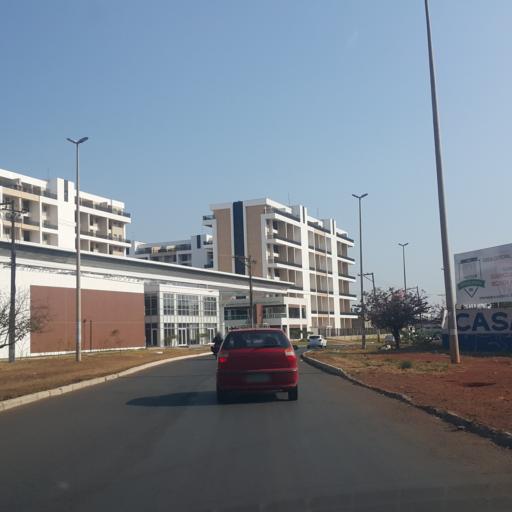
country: BR
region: Federal District
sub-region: Brasilia
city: Brasilia
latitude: -15.8658
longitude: -48.0340
